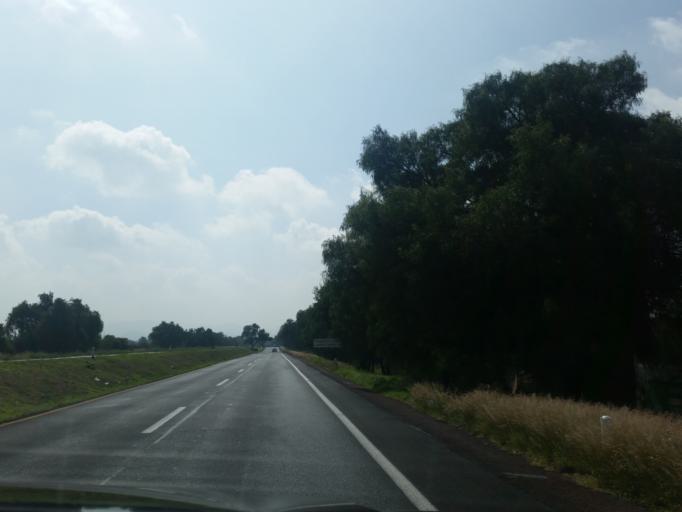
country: MX
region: Mexico
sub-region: Acolman de Nezahualcoyotl
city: Prados de San Juan
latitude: 19.6211
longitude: -98.9678
